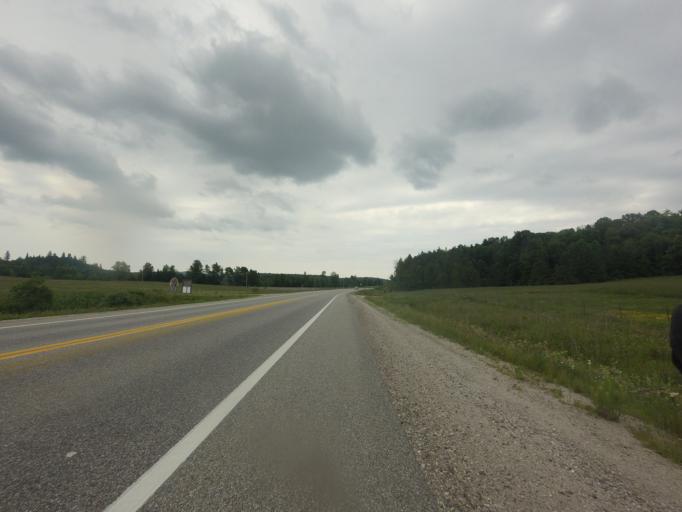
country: CA
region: Quebec
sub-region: Outaouais
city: Wakefield
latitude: 45.7251
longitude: -75.9107
